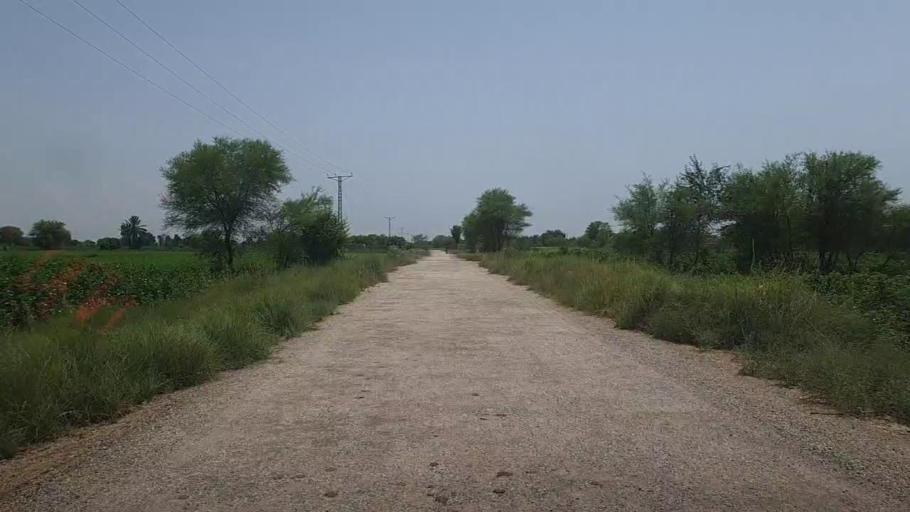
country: PK
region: Sindh
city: Pad Idan
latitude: 26.8376
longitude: 68.3248
